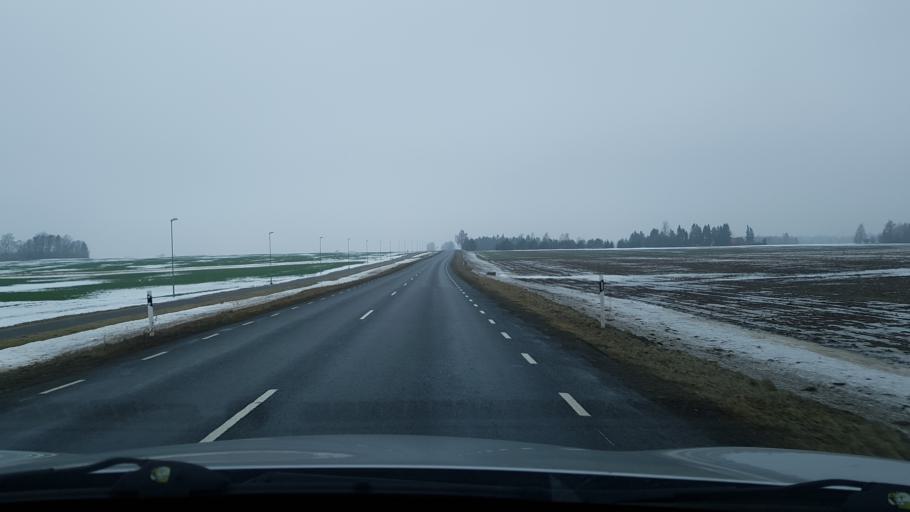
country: EE
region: Valgamaa
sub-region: Torva linn
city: Torva
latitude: 58.2170
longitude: 25.9091
